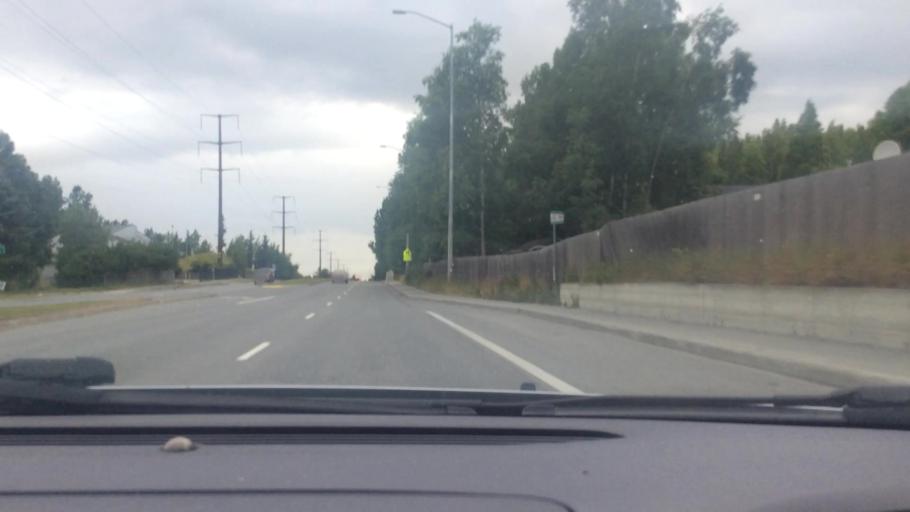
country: US
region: Alaska
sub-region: Anchorage Municipality
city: Anchorage
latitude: 61.1953
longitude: -149.7690
